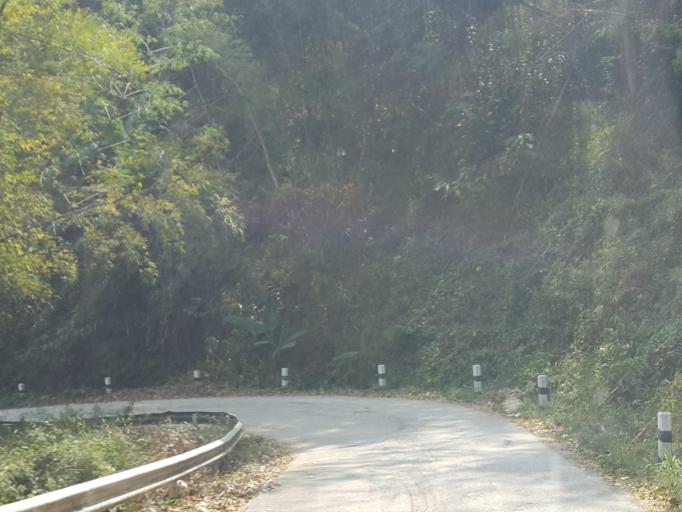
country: TH
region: Chiang Mai
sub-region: Amphoe Chiang Dao
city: Chiang Dao
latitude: 19.4143
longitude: 98.8561
